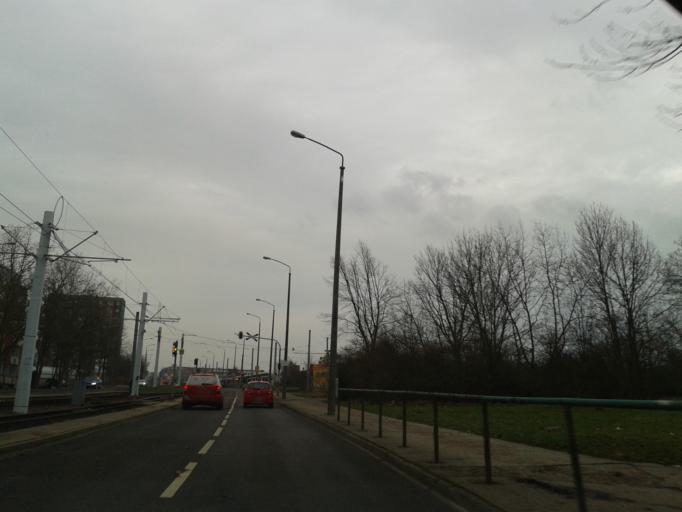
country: DE
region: Saxony-Anhalt
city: Angersdorf
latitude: 51.4502
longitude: 11.9465
